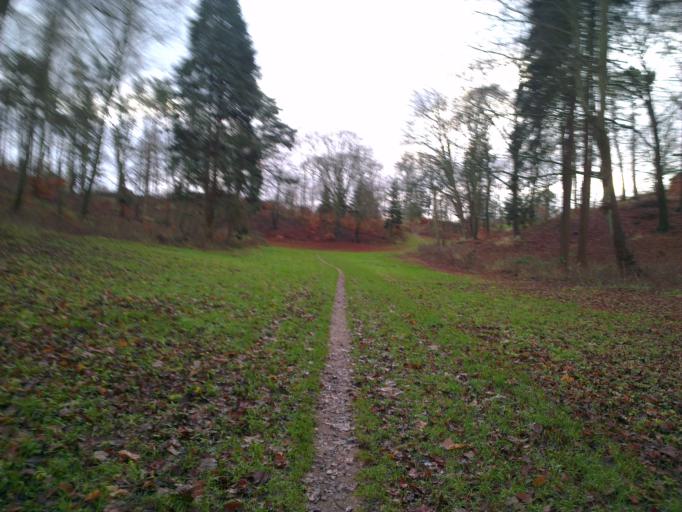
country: DK
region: Capital Region
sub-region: Frederikssund Kommune
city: Jaegerspris
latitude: 55.8522
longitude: 12.0059
